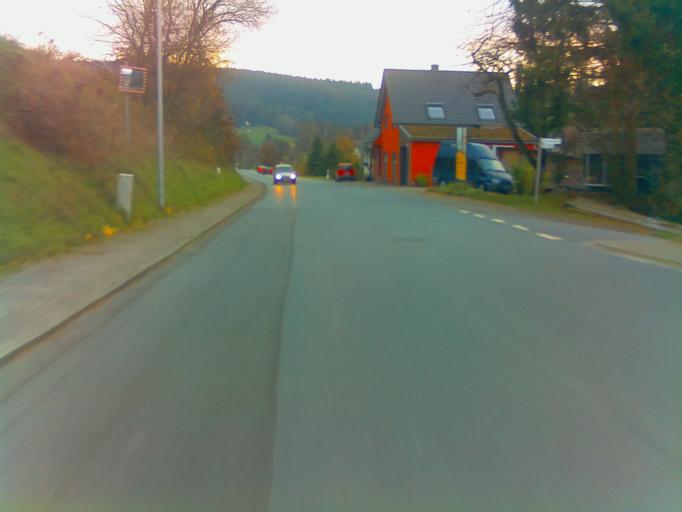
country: DE
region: Hesse
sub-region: Regierungsbezirk Darmstadt
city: Beerfelden
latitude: 49.5875
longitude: 8.9278
